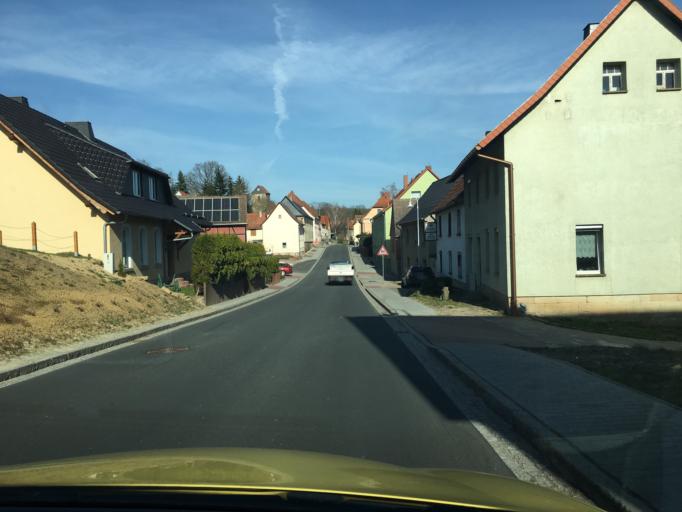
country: DE
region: Saxony-Anhalt
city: Bad Bibra
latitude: 51.2145
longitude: 11.5215
